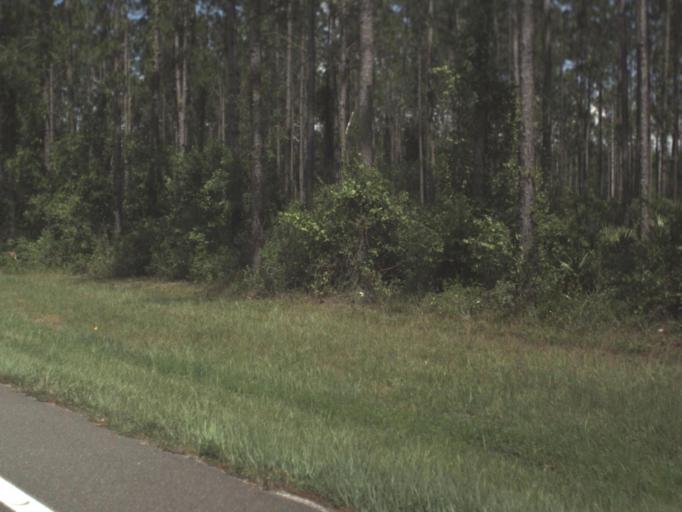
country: US
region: Florida
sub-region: Alachua County
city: Waldo
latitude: 29.6990
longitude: -82.1825
